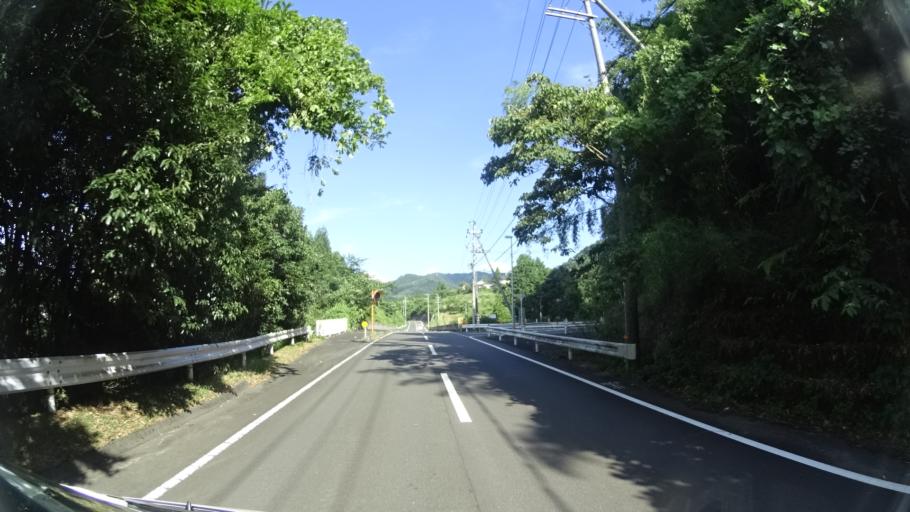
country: JP
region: Kyoto
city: Ayabe
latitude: 35.2863
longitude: 135.2873
